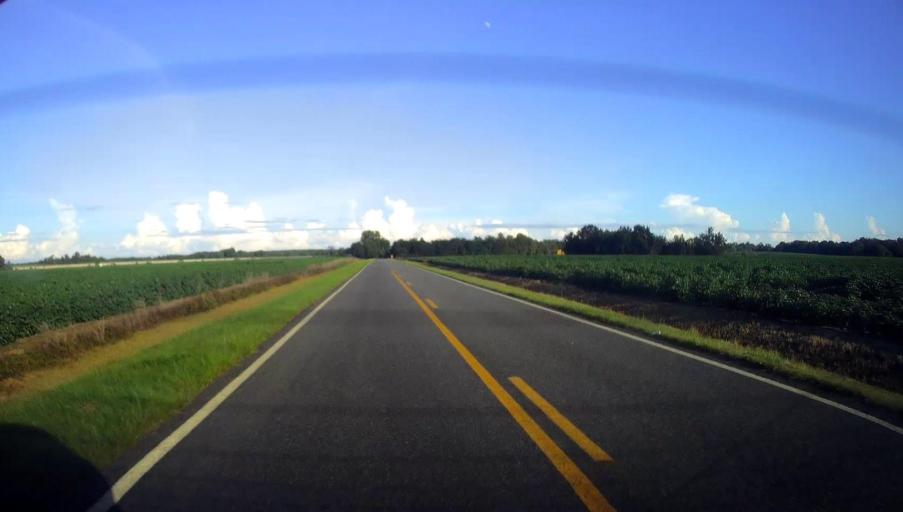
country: US
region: Georgia
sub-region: Pulaski County
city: Hawkinsville
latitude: 32.2859
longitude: -83.5432
